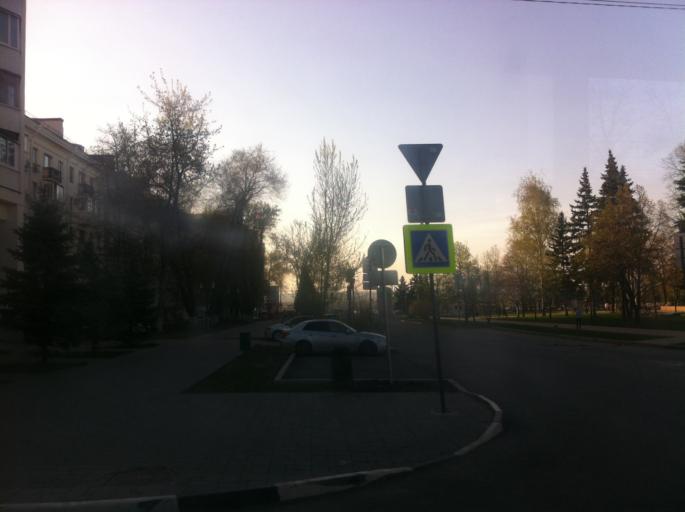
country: RU
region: Samara
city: Samara
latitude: 53.2018
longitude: 50.1125
